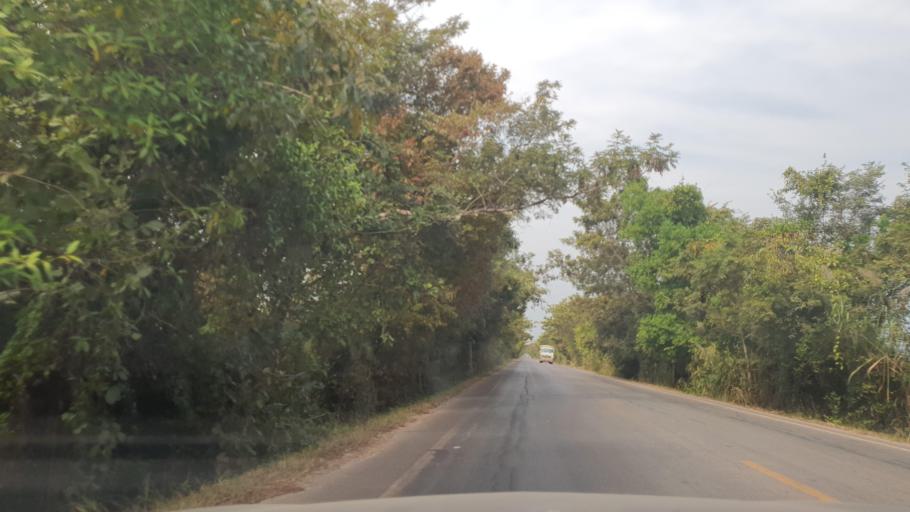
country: TH
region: Changwat Bueng Kan
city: Bung Khla
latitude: 18.2170
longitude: 104.0405
